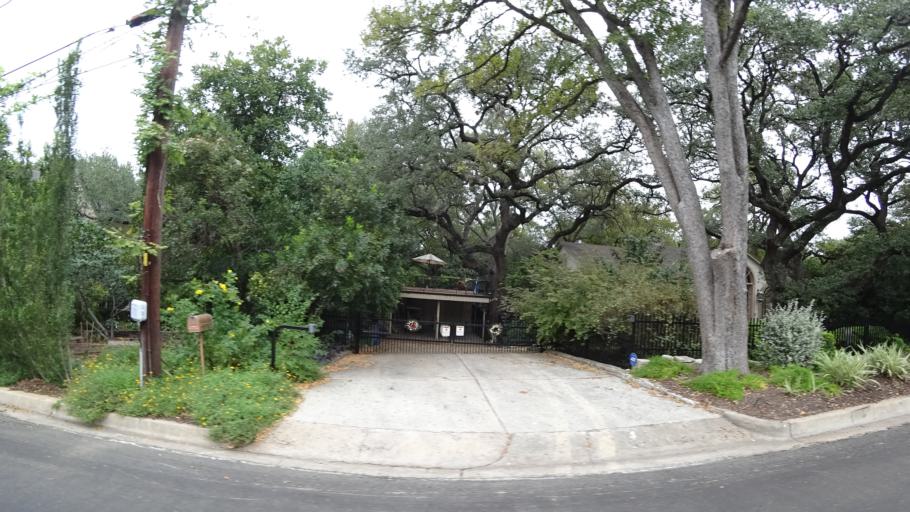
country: US
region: Texas
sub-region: Travis County
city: Austin
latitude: 30.2960
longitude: -97.7259
